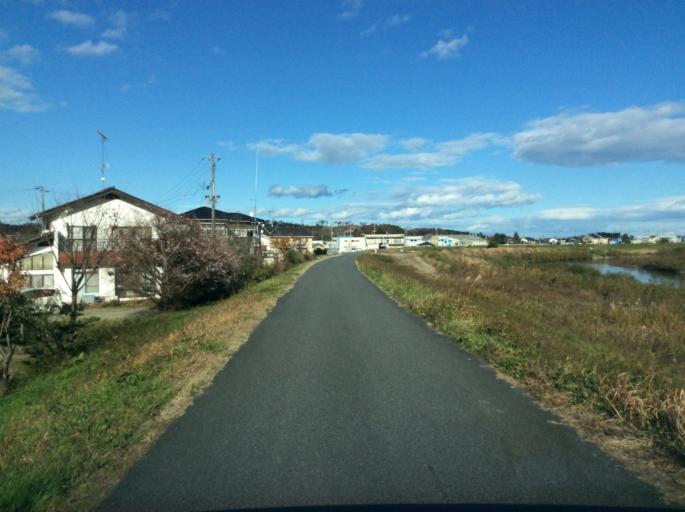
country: JP
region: Fukushima
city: Iwaki
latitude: 37.0578
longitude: 140.9238
